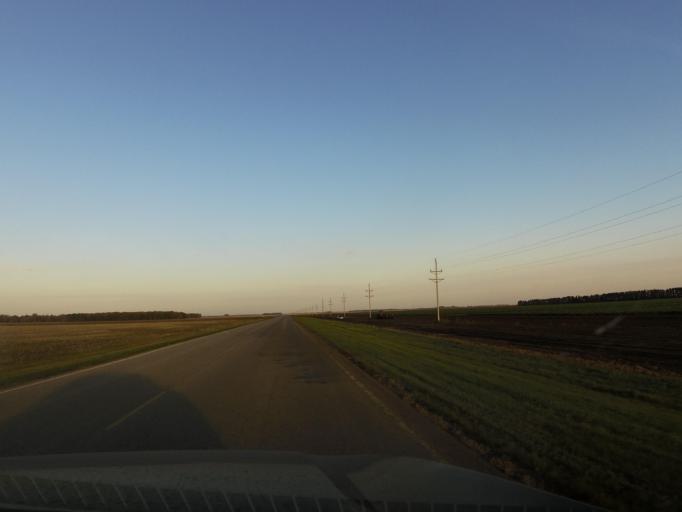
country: CA
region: Manitoba
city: Altona
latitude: 48.9634
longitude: -97.6559
